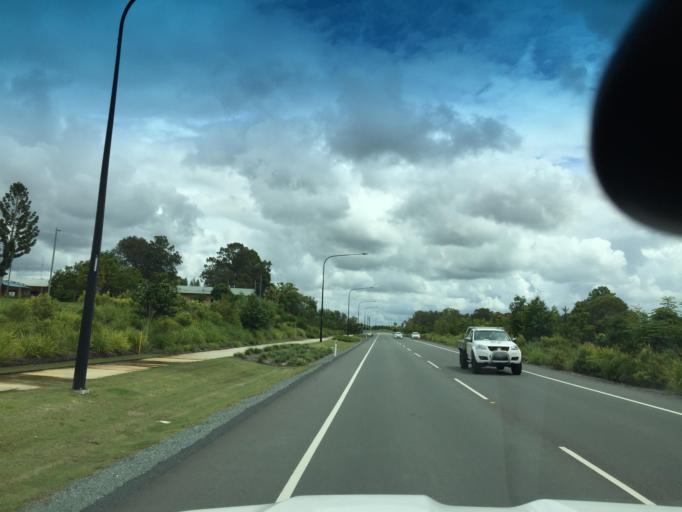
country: AU
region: Queensland
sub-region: Moreton Bay
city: Caboolture South
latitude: -27.1007
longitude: 152.9691
